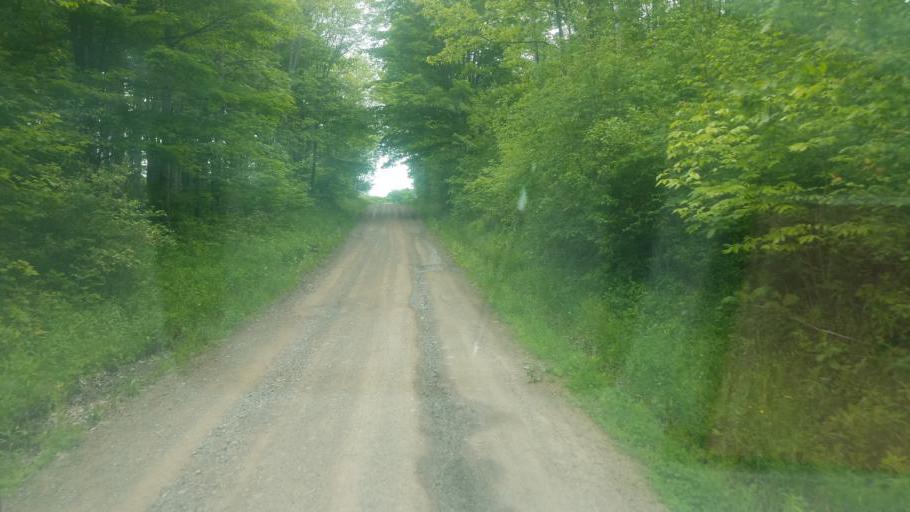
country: US
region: Pennsylvania
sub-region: Tioga County
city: Westfield
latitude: 41.9304
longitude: -77.6959
